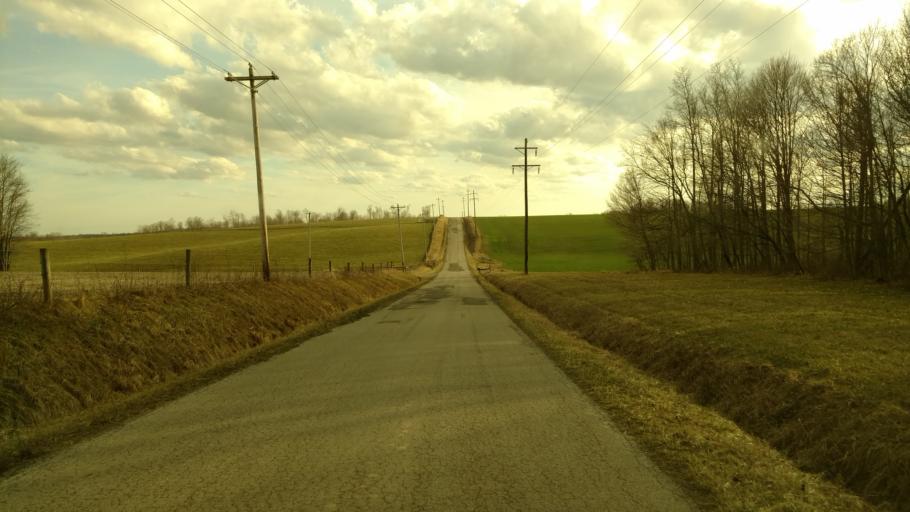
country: US
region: Ohio
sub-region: Knox County
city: Fredericktown
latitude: 40.5335
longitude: -82.4490
